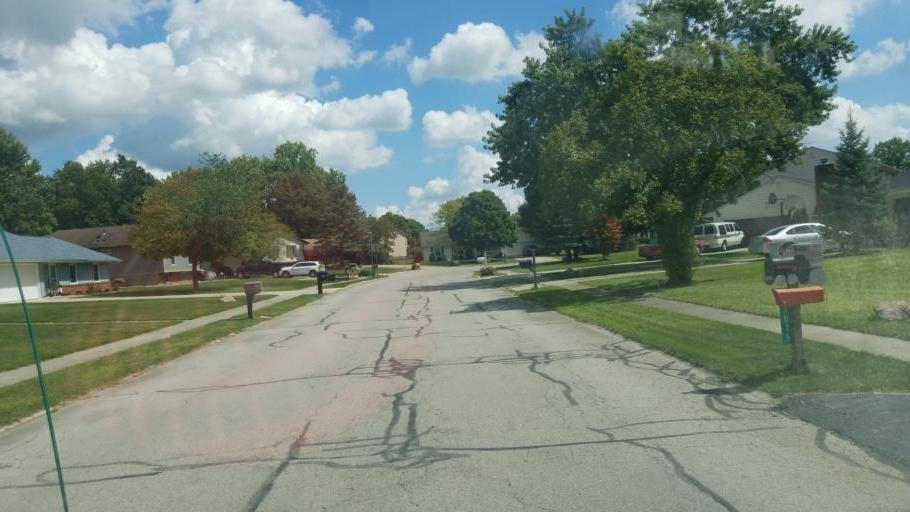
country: US
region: Ohio
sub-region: Marion County
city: Marion
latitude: 40.5708
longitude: -83.0983
